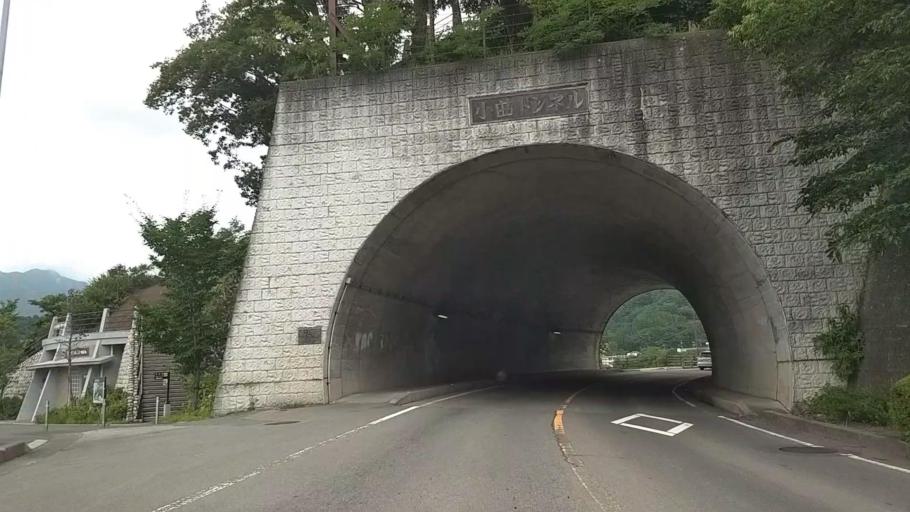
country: JP
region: Yamanashi
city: Fujikawaguchiko
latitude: 35.5061
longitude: 138.7722
